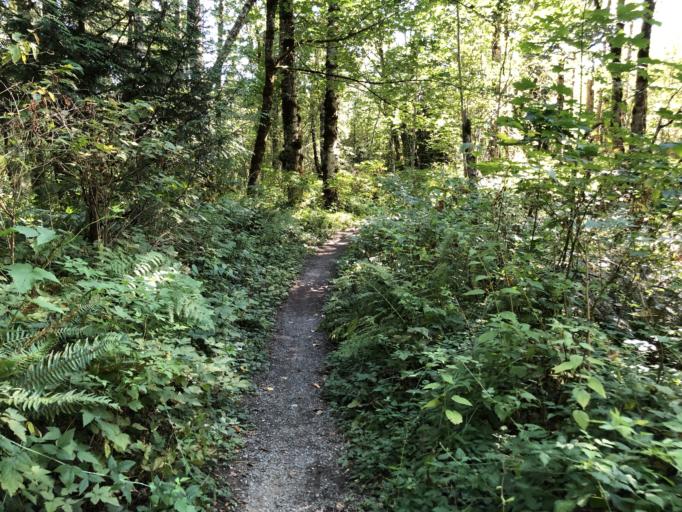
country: US
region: Washington
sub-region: King County
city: Ames Lake
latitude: 47.5900
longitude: -121.9776
